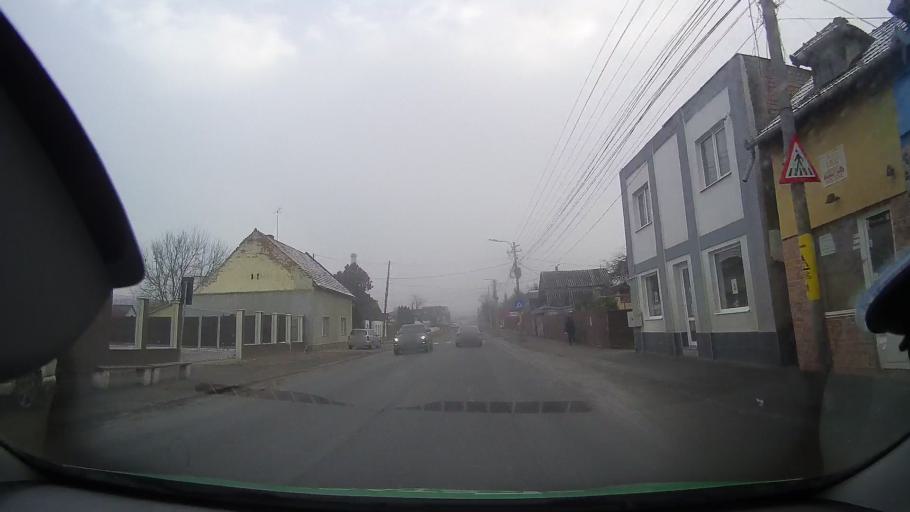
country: RO
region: Mures
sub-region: Municipiul Tarnaveni
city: Tarnaveni
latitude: 46.3185
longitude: 24.2967
